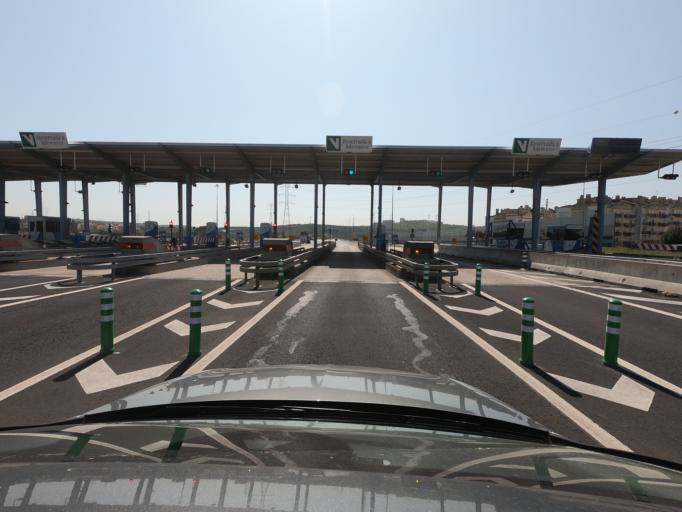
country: PT
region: Lisbon
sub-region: Sintra
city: Belas
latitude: 38.7711
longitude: -9.2754
